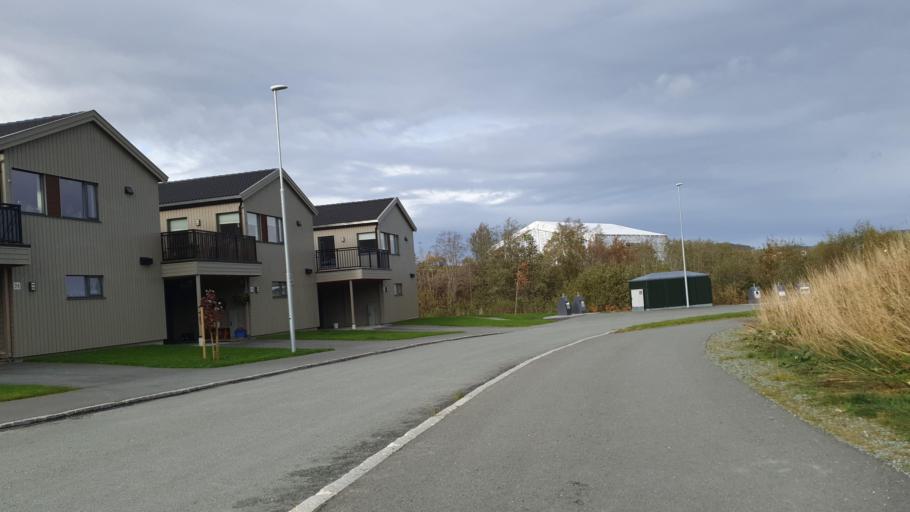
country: NO
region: Sor-Trondelag
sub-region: Klaebu
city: Klaebu
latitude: 63.3041
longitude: 10.4686
